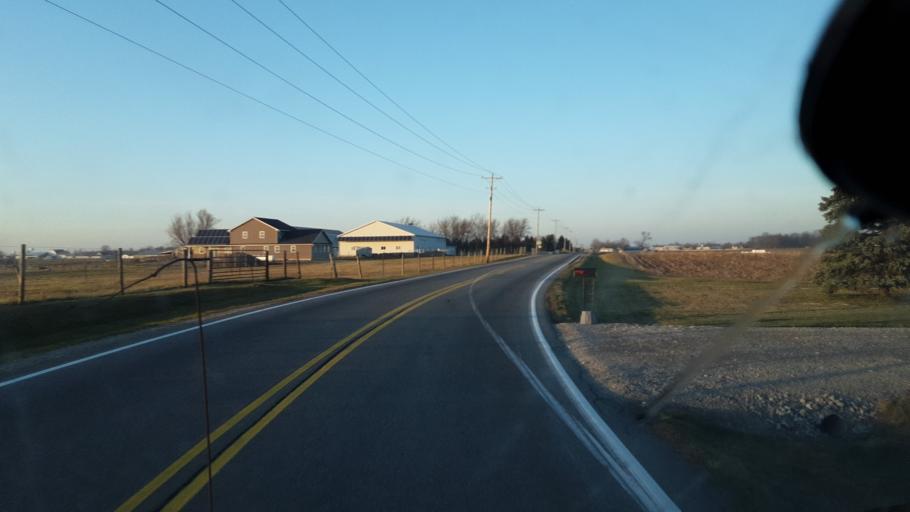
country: US
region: Indiana
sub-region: Allen County
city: Harlan
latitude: 41.1878
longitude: -84.9410
